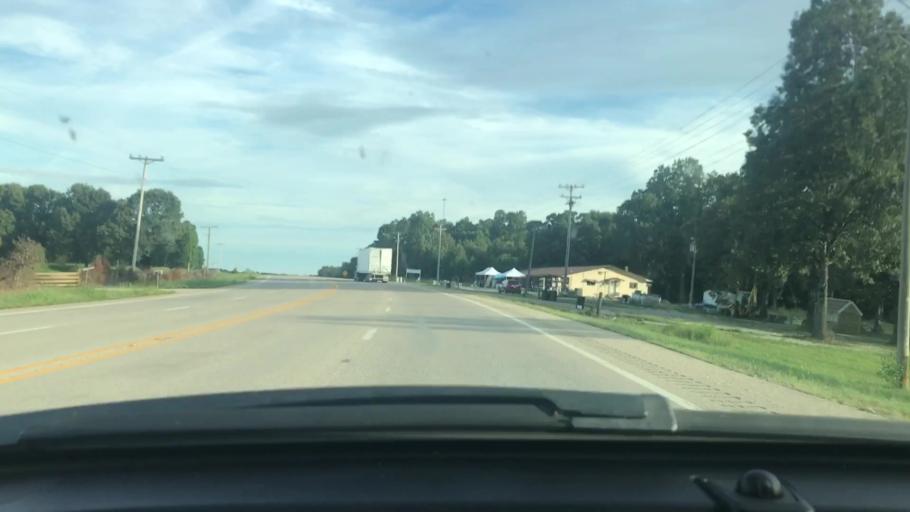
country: US
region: Arkansas
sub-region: Lawrence County
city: Hoxie
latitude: 36.1287
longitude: -91.1576
